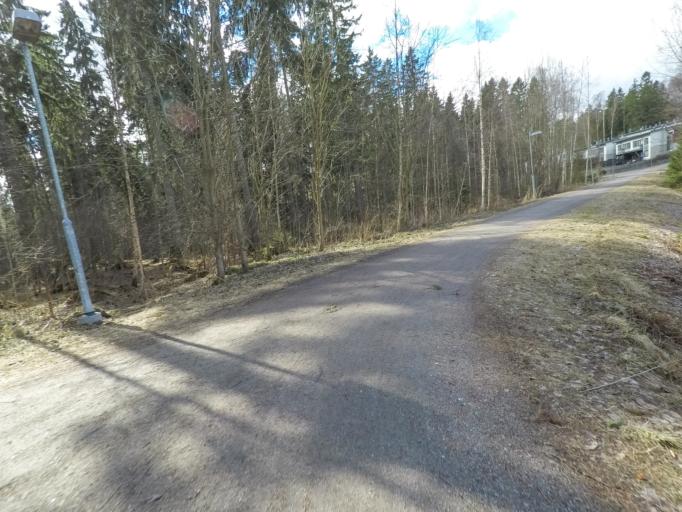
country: FI
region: Uusimaa
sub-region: Helsinki
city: Vantaa
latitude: 60.2232
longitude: 25.0506
